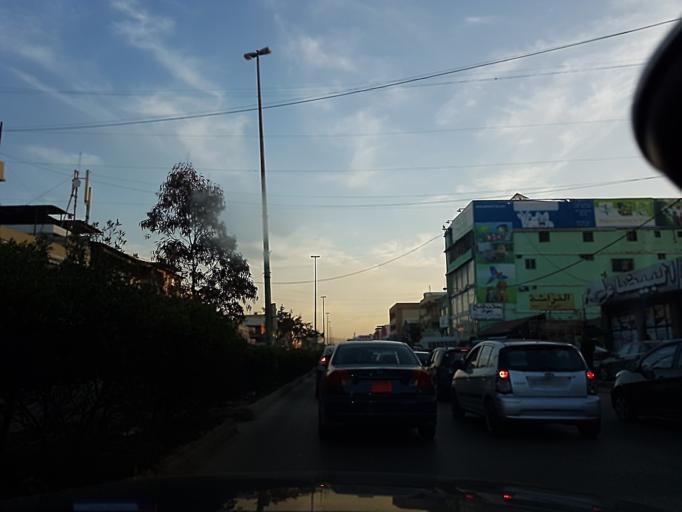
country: LB
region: Beyrouth
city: Beirut
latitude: 33.8413
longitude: 35.4848
